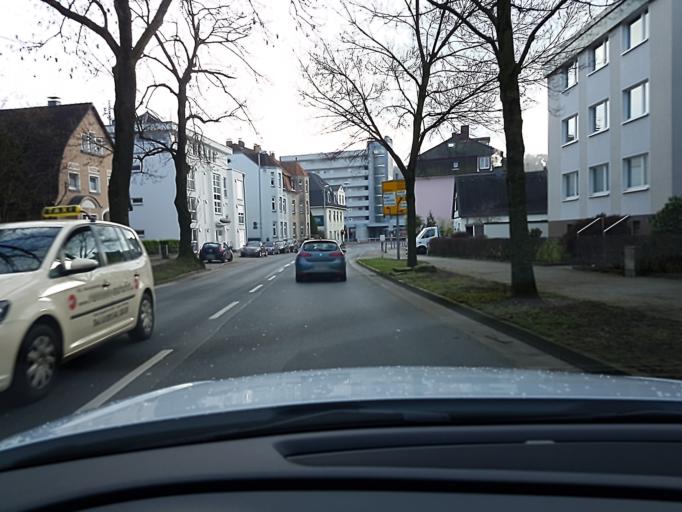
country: DE
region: North Rhine-Westphalia
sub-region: Regierungsbezirk Dusseldorf
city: Heiligenhaus
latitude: 51.3633
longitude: 6.9458
